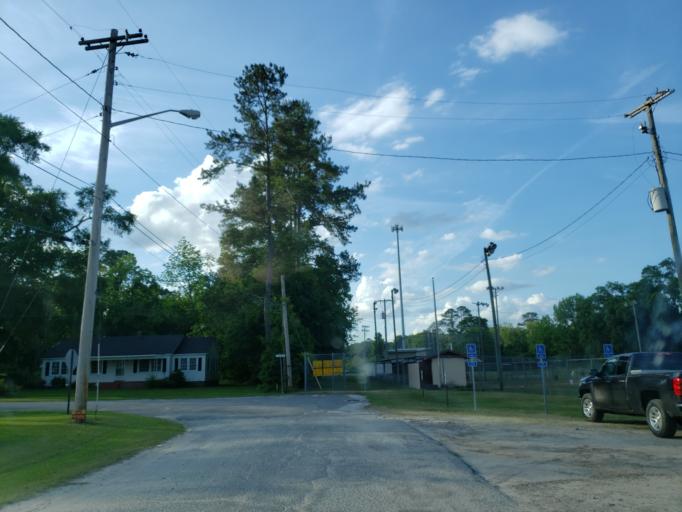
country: US
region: Georgia
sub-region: Cook County
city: Adel
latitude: 31.1394
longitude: -83.4185
